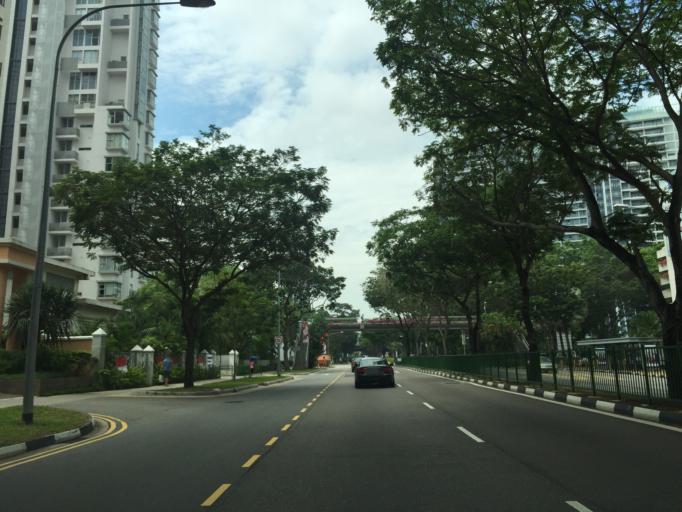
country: SG
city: Singapore
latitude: 1.3179
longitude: 103.8442
